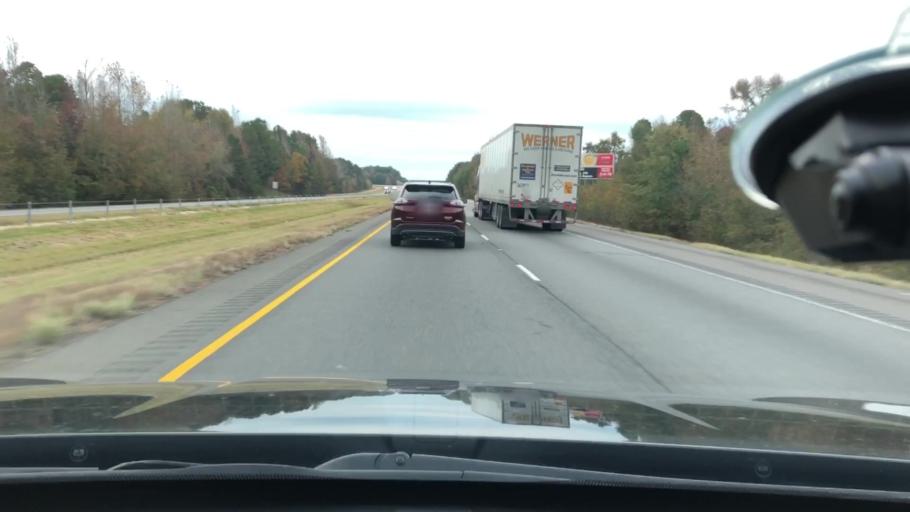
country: US
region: Arkansas
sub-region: Clark County
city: Arkadelphia
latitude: 34.0644
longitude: -93.1256
